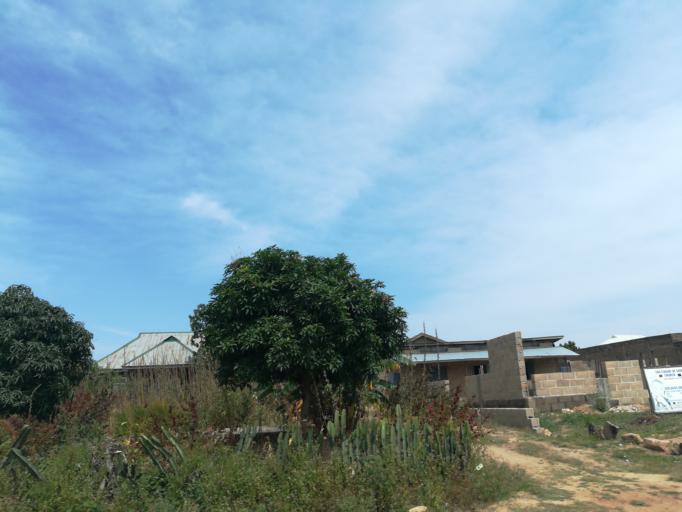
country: NG
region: Plateau
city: Jos
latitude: 9.9234
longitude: 8.8355
